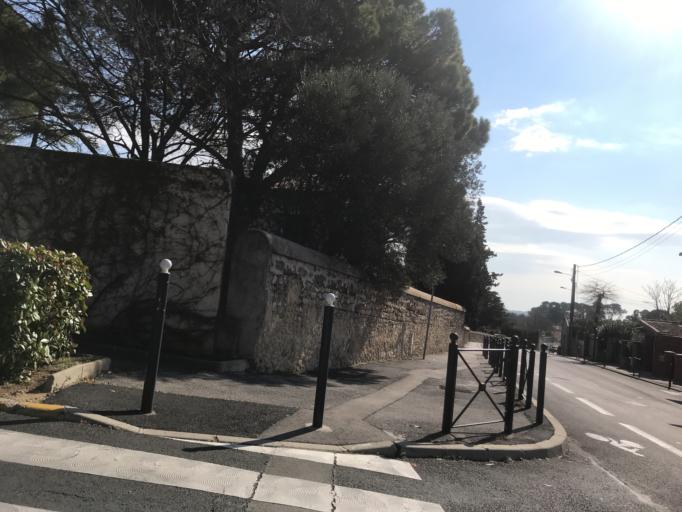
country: FR
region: Languedoc-Roussillon
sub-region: Departement de l'Herault
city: Montferrier-sur-Lez
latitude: 43.6400
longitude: 3.8587
